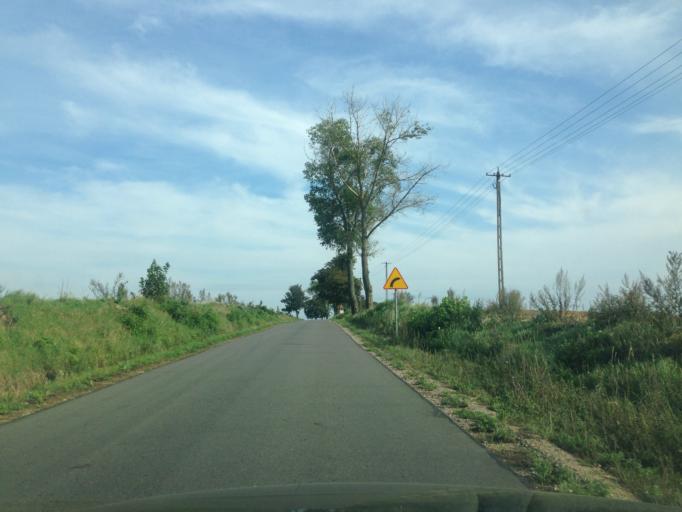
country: PL
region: Kujawsko-Pomorskie
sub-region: Powiat brodnicki
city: Bartniczka
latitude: 53.2540
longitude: 19.6532
